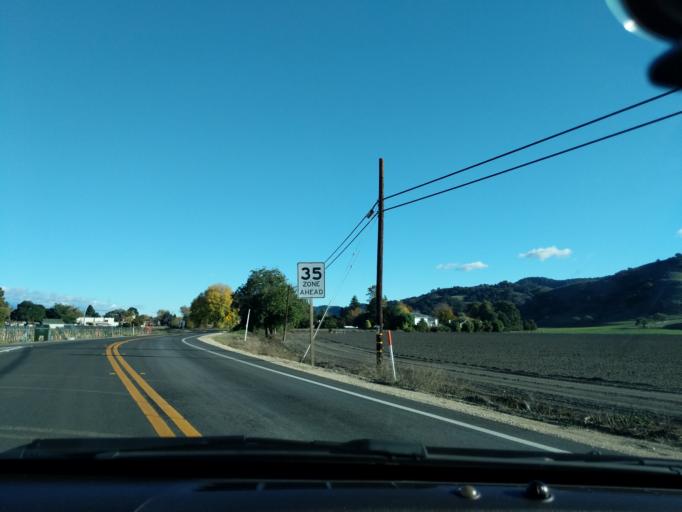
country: US
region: California
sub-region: Santa Barbara County
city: Los Alamos
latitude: 34.7453
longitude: -120.2871
